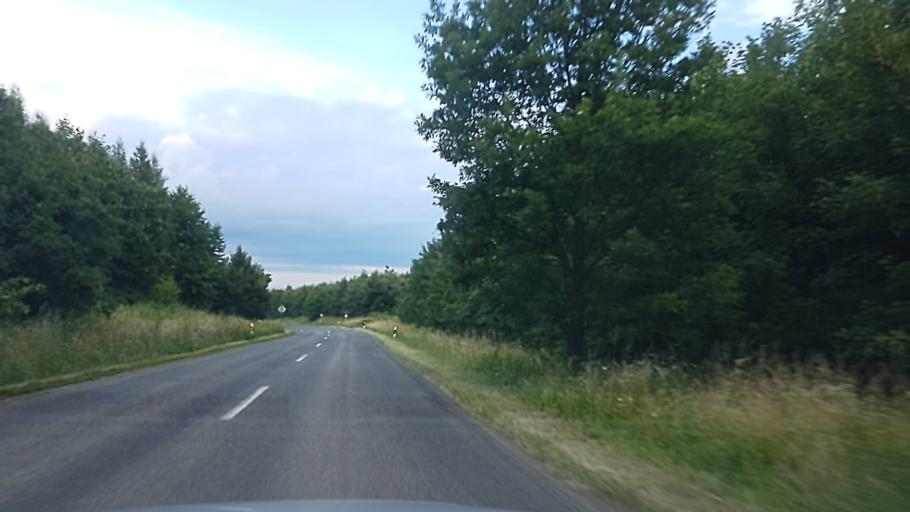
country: HU
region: Somogy
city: Kaposvar
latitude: 46.2642
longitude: 17.8263
